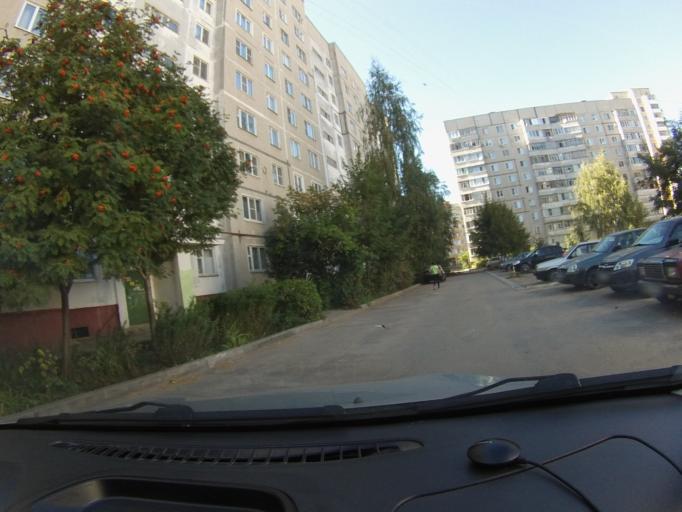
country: RU
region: Tambov
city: Tambov
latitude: 52.7657
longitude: 41.4025
